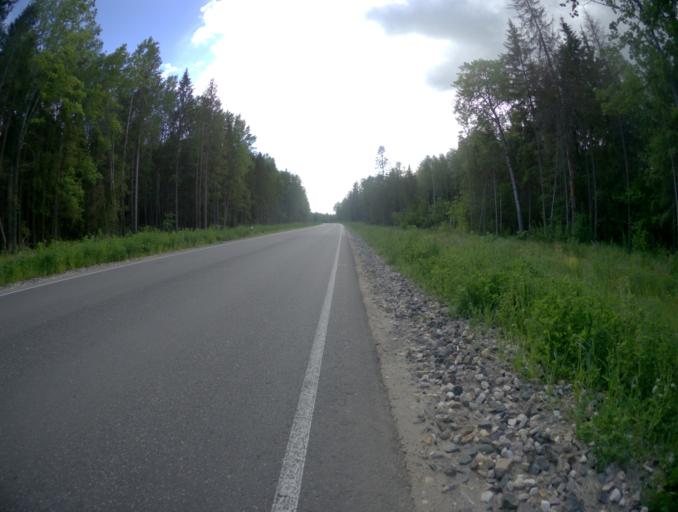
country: RU
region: Ivanovo
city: Kitovo
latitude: 56.8031
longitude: 41.1776
